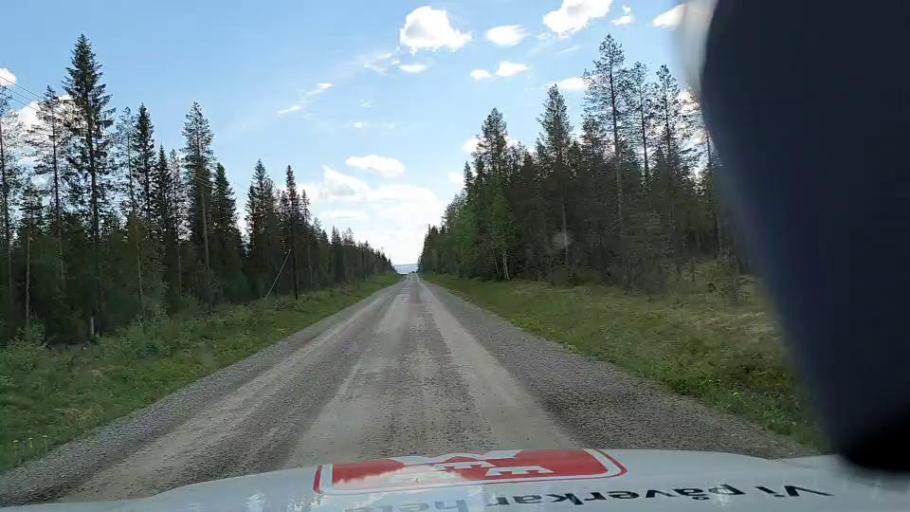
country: SE
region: Jaemtland
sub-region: Stroemsunds Kommun
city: Stroemsund
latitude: 64.5275
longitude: 15.5916
